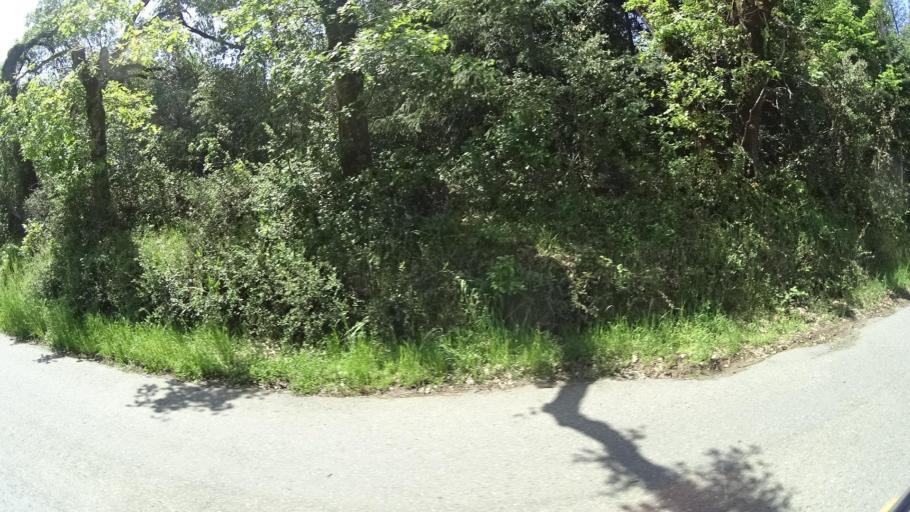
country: US
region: California
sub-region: Humboldt County
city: Redway
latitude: 40.1733
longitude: -123.6098
